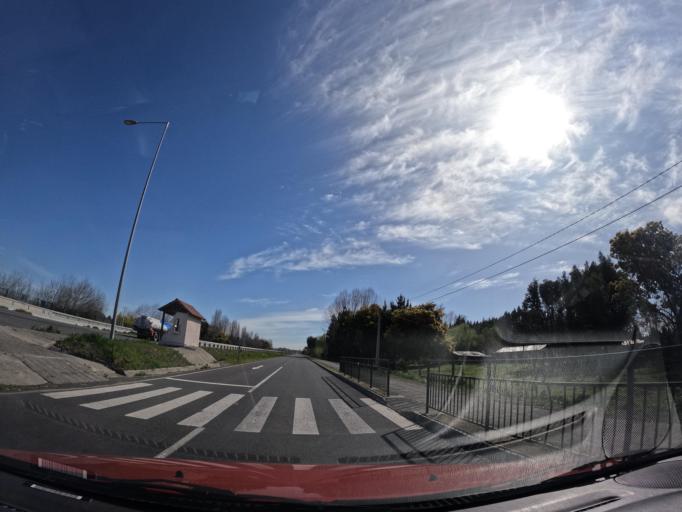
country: CL
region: Biobio
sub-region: Provincia de Biobio
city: Cabrero
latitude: -37.0267
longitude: -72.4471
